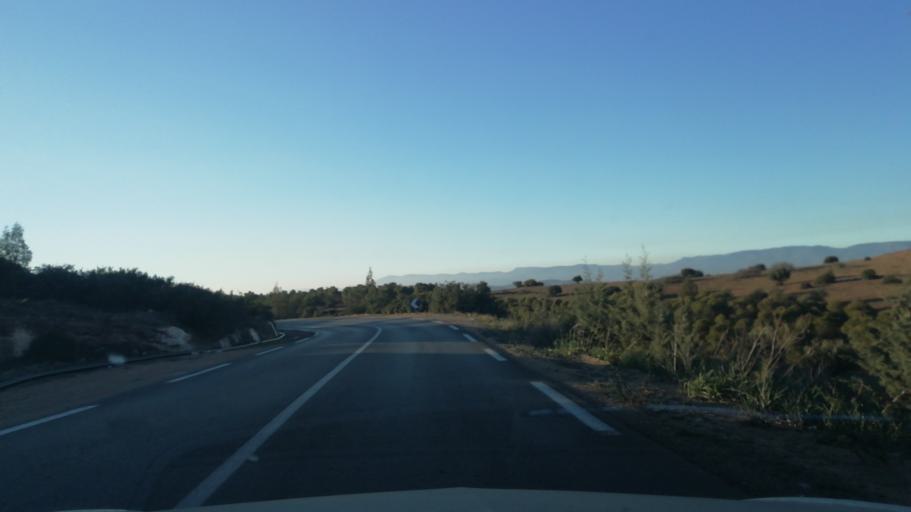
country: DZ
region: Tlemcen
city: Beni Mester
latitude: 34.8154
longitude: -1.6179
